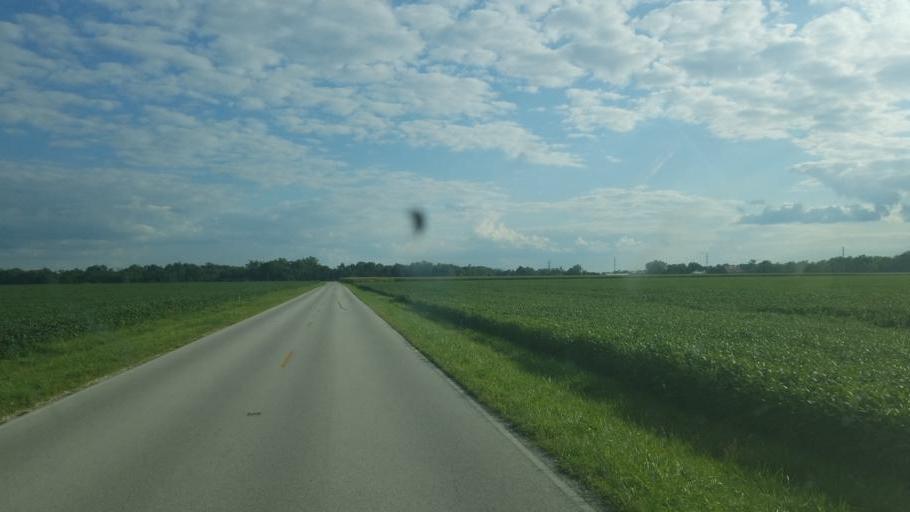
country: US
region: Ohio
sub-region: Seneca County
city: Tiffin
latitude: 41.1735
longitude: -83.1227
